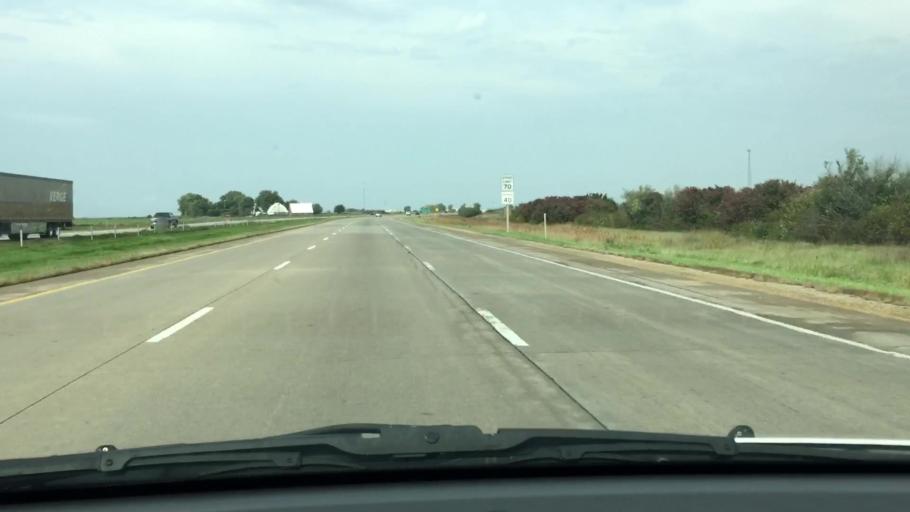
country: US
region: Iowa
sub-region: Scott County
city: Walcott
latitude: 41.6187
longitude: -90.7931
